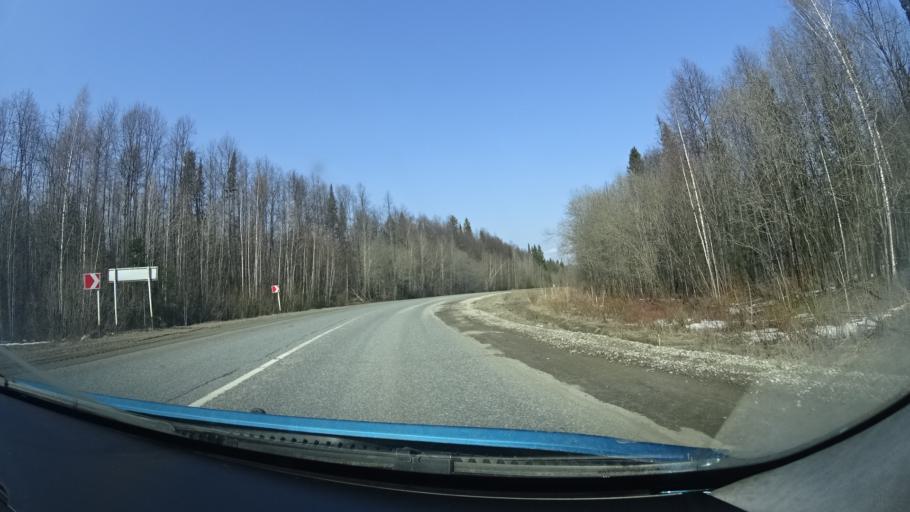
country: RU
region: Perm
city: Yugo-Kamskiy
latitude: 57.5079
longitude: 55.6851
